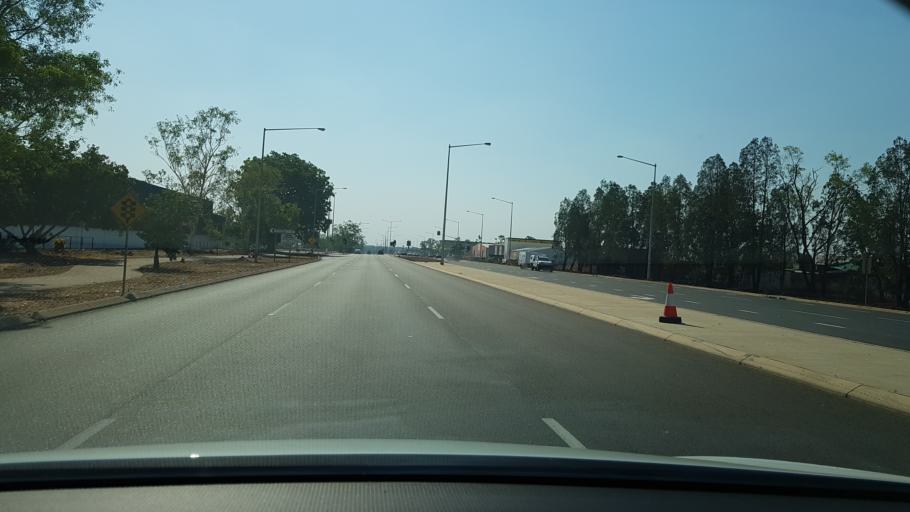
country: AU
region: Northern Territory
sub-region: Palmerston
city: Palmerston
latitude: -12.4775
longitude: 130.9868
